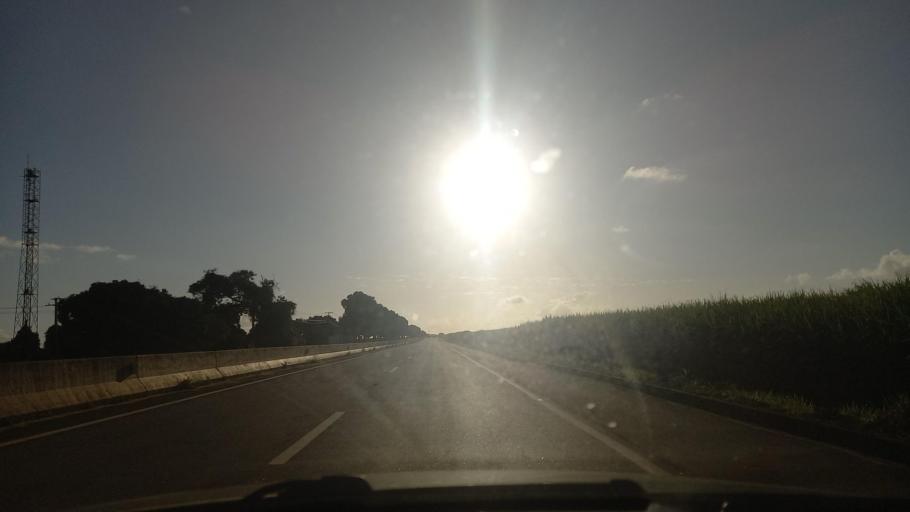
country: BR
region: Alagoas
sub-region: Campo Alegre
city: Campo Alegre
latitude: -9.7968
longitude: -36.3020
